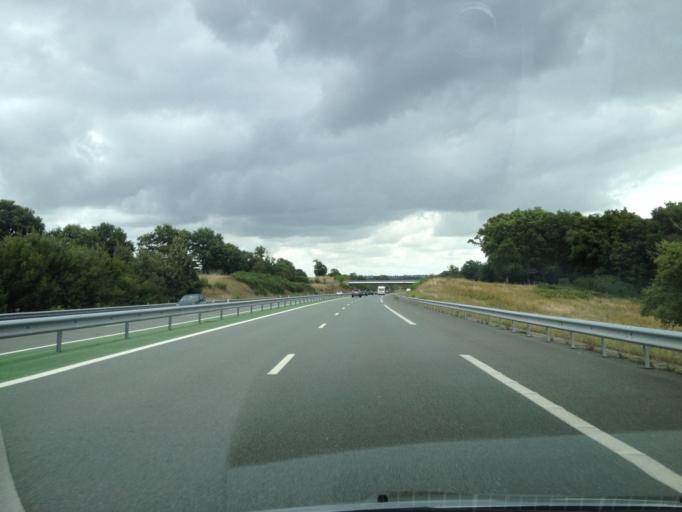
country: FR
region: Pays de la Loire
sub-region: Departement de la Vendee
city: Mortagne-sur-Sevre
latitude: 46.9563
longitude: -0.9375
